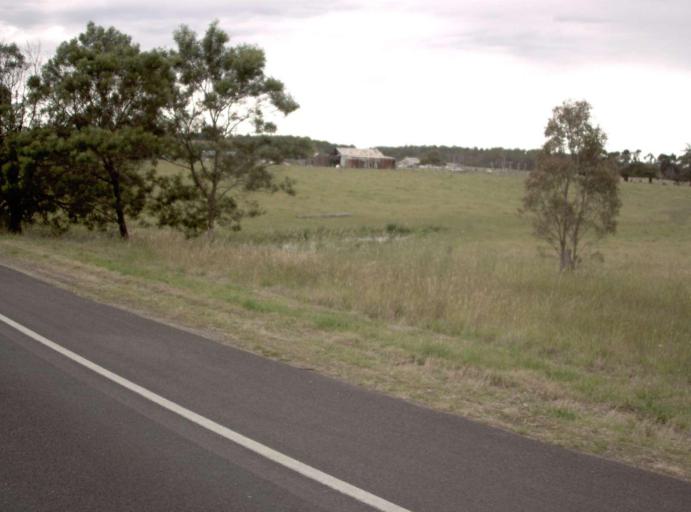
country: AU
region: Victoria
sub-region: Wellington
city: Sale
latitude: -38.2990
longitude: 147.0333
